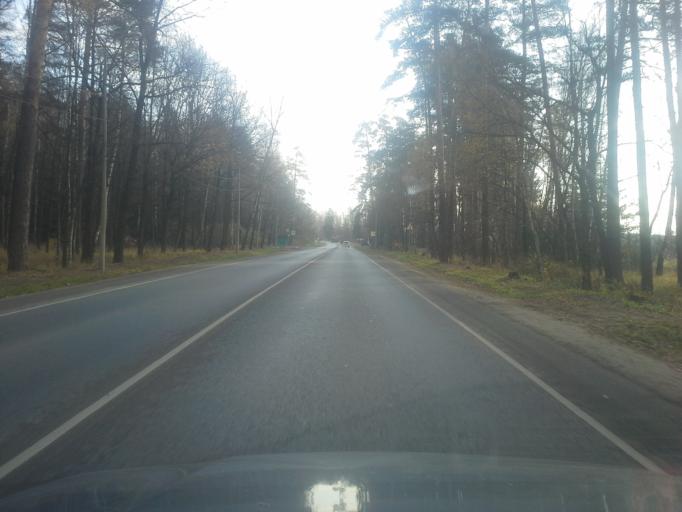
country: RU
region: Moskovskaya
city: Bol'shiye Vyazemy
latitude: 55.6698
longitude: 36.9529
